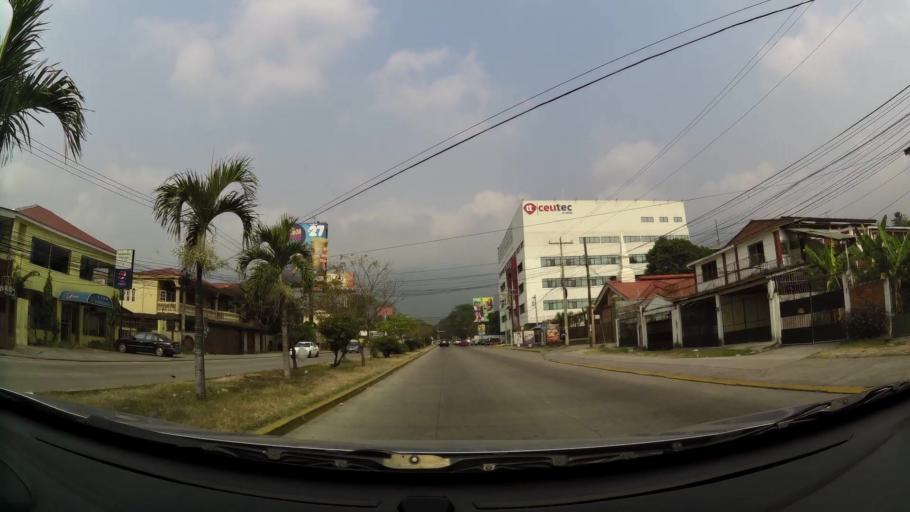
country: HN
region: Cortes
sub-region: San Pedro Sula
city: Pena Blanca
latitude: 15.5300
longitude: -88.0311
